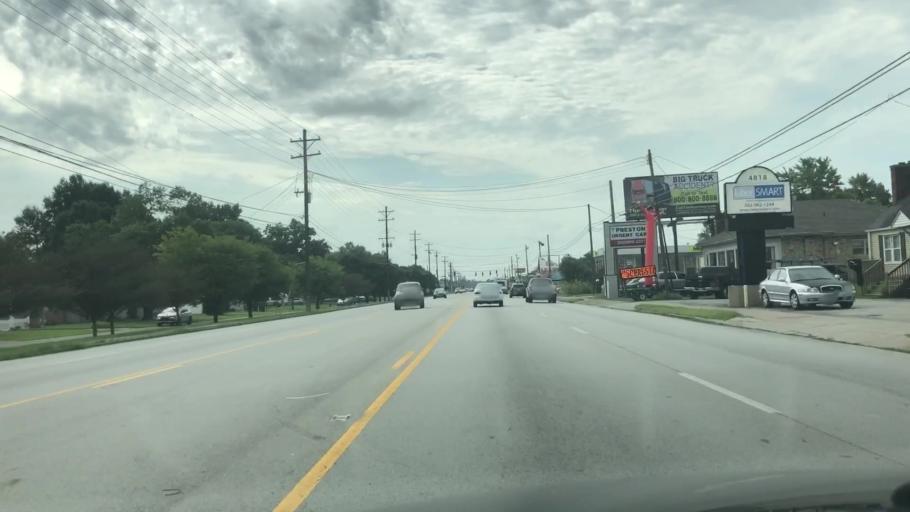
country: US
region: Kentucky
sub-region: Jefferson County
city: Audubon Park
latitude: 38.1778
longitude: -85.7161
